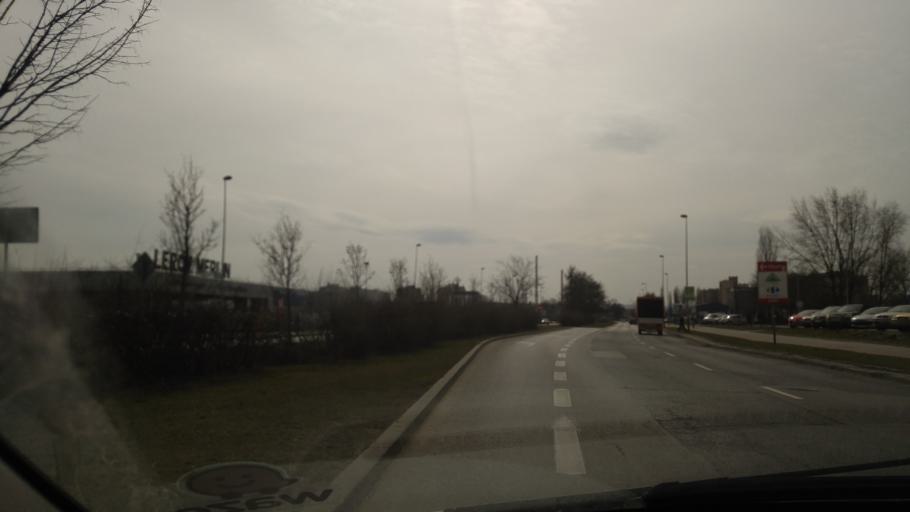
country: PL
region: Lesser Poland Voivodeship
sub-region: Krakow
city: Krakow
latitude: 50.0794
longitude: 20.0153
